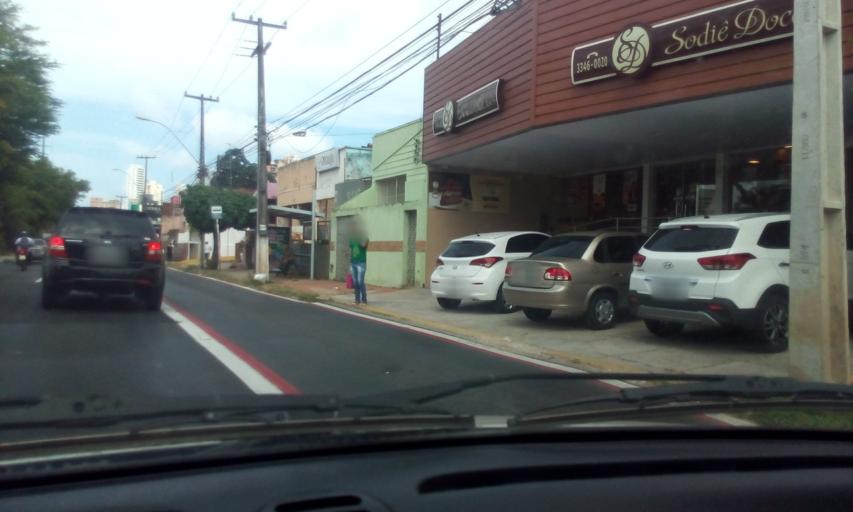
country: BR
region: Rio Grande do Norte
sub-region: Natal
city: Natal
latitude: -5.7993
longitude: -35.2055
